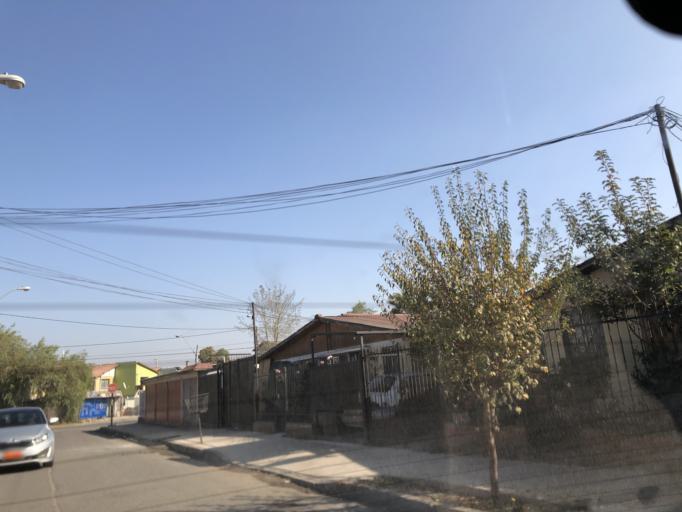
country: CL
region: Santiago Metropolitan
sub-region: Provincia de Cordillera
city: Puente Alto
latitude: -33.6306
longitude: -70.5924
